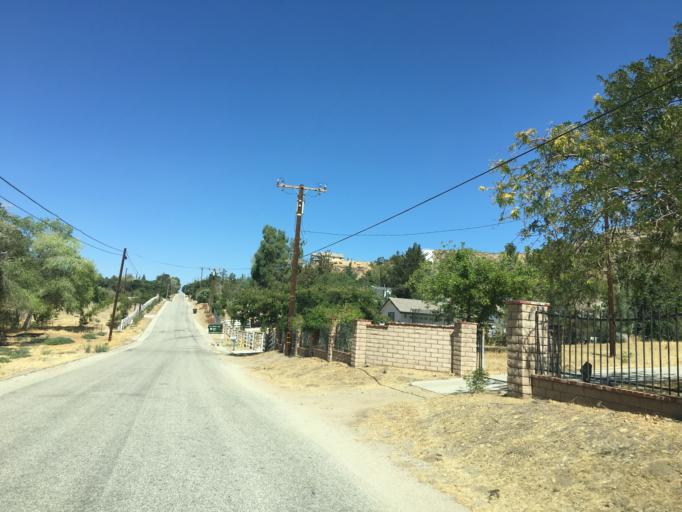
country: US
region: California
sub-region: Los Angeles County
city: Leona Valley
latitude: 34.6259
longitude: -118.2975
